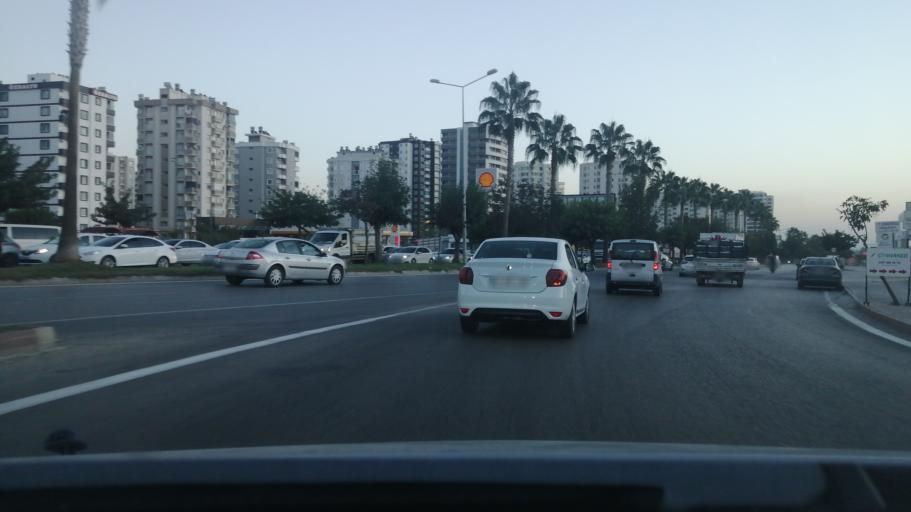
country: TR
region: Adana
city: Seyhan
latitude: 37.0233
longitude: 35.2535
